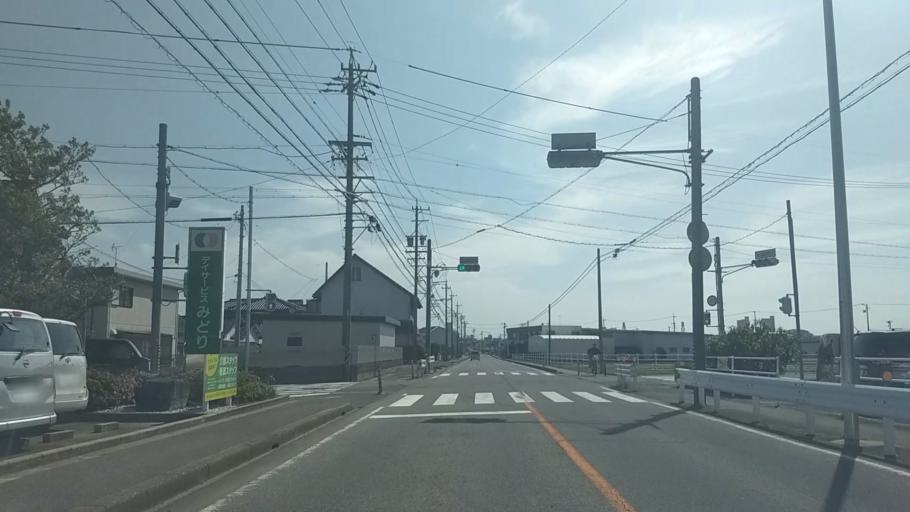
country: JP
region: Aichi
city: Anjo
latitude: 34.9685
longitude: 137.1032
